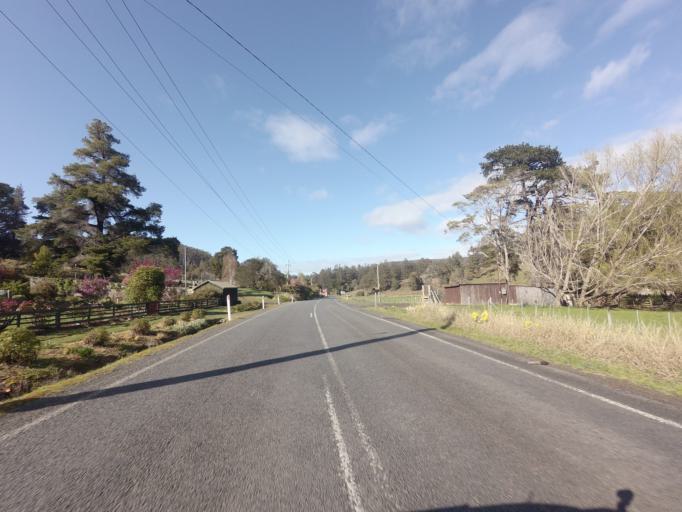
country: AU
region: Tasmania
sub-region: Huon Valley
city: Cygnet
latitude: -43.2679
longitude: 147.0111
